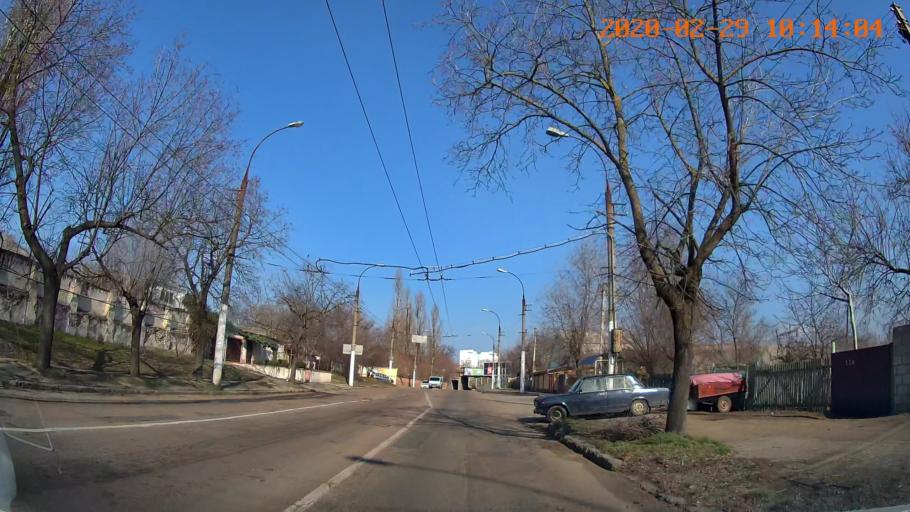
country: MD
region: Telenesti
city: Tiraspolul Nou
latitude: 46.8437
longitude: 29.6446
